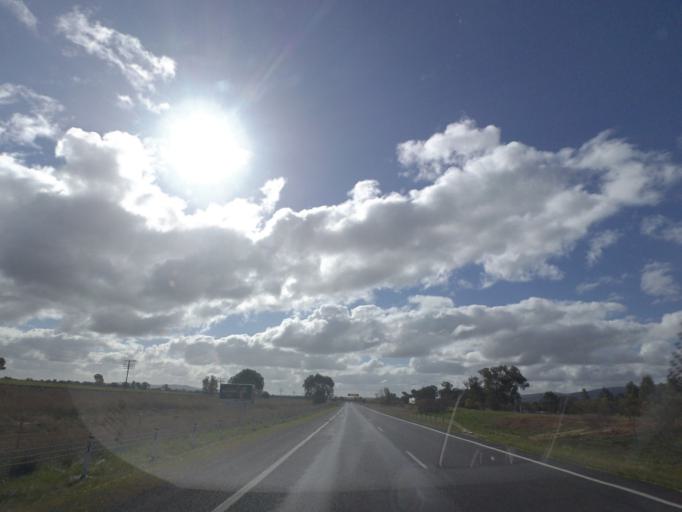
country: AU
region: New South Wales
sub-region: Greater Hume Shire
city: Jindera
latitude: -35.9479
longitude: 147.0036
